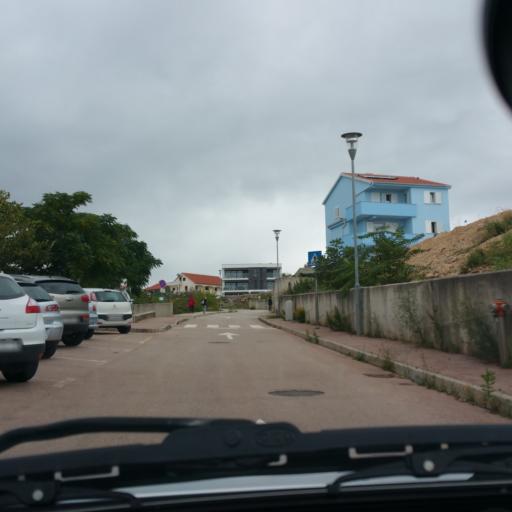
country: HR
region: Primorsko-Goranska
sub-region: Grad Krk
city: Krk
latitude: 45.0299
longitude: 14.5696
